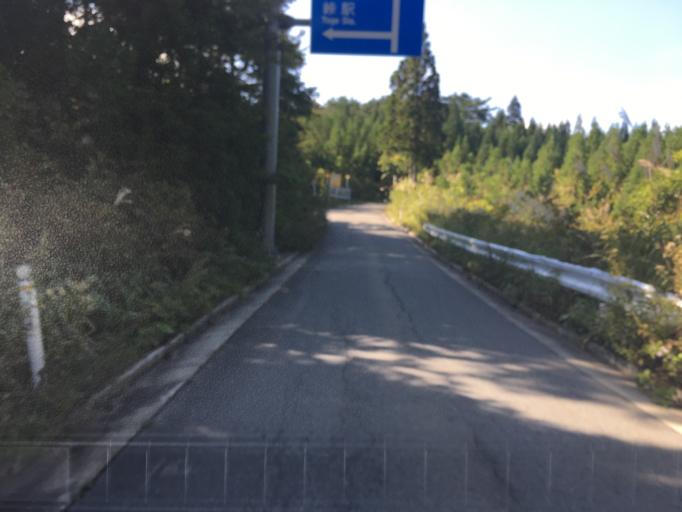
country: JP
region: Yamagata
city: Yonezawa
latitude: 37.8118
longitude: 140.2522
